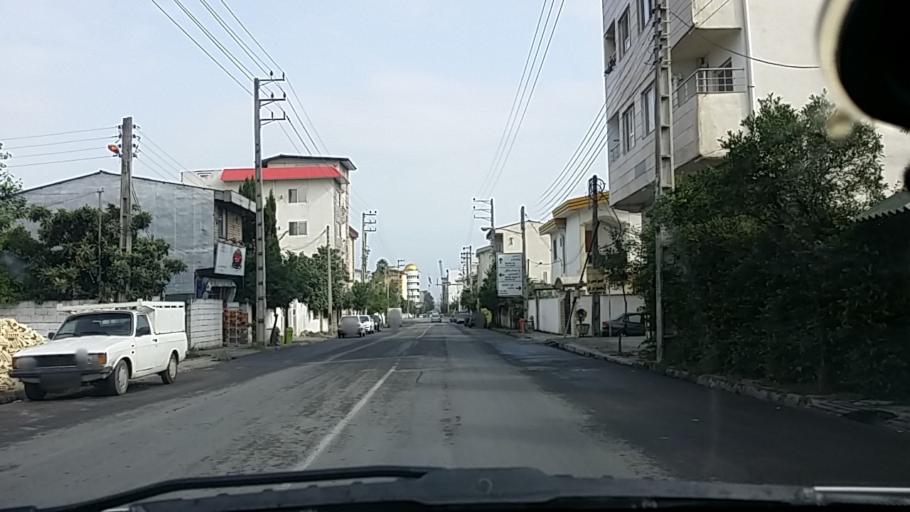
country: IR
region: Mazandaran
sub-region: Nowshahr
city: Nowshahr
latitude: 36.6451
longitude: 51.5084
